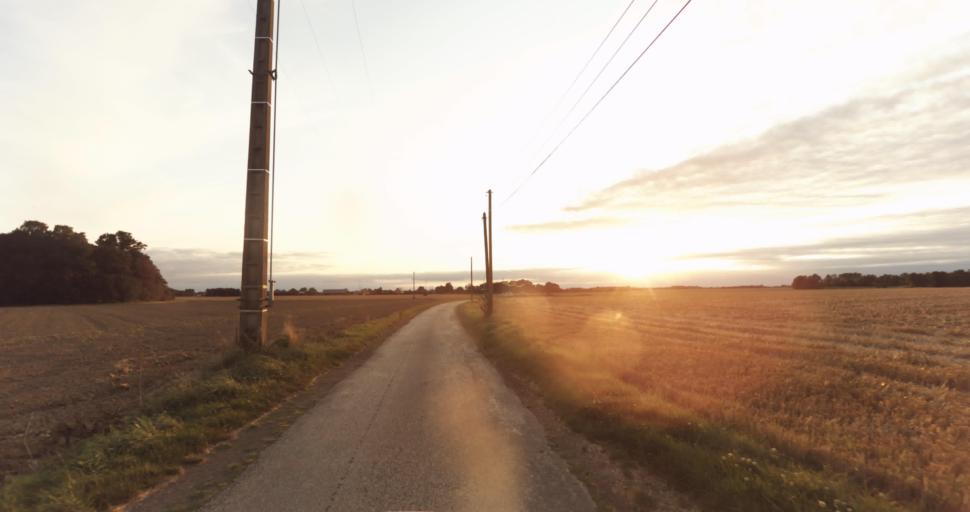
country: FR
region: Haute-Normandie
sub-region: Departement de l'Eure
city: La Madeleine-de-Nonancourt
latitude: 48.8757
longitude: 1.1961
